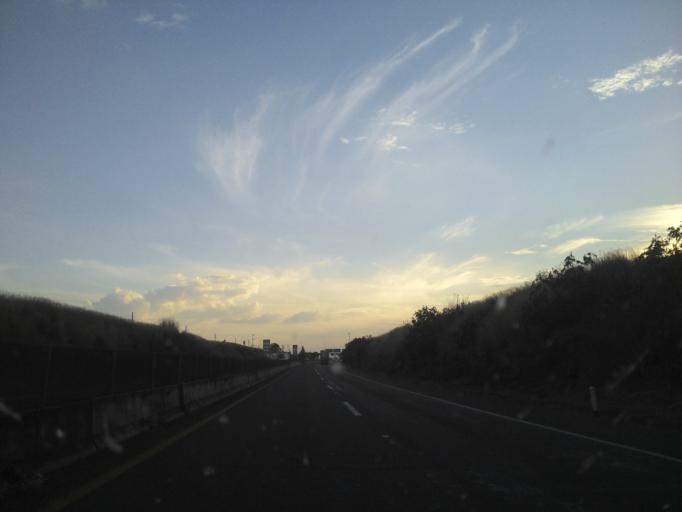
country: MX
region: Jalisco
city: Tepatitlan de Morelos
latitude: 20.8292
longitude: -102.7926
